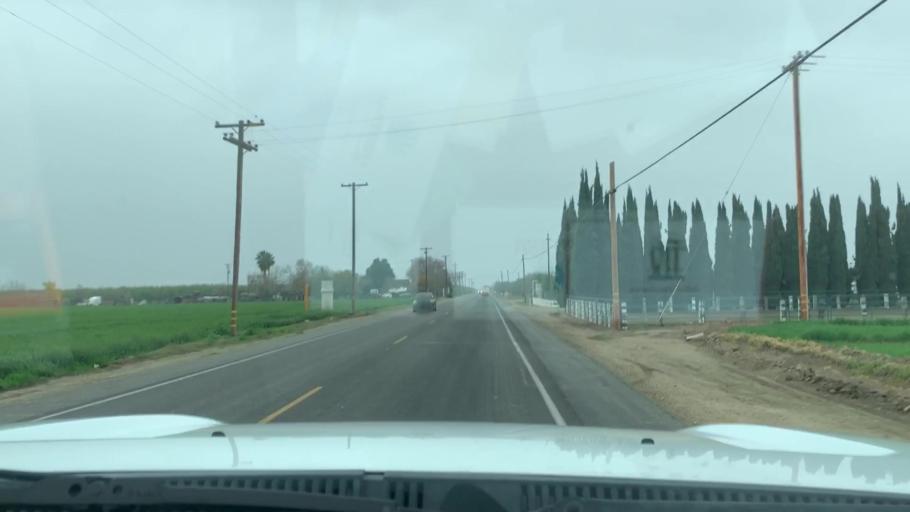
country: US
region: California
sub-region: Kern County
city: Shafter
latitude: 35.5000
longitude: -119.3203
